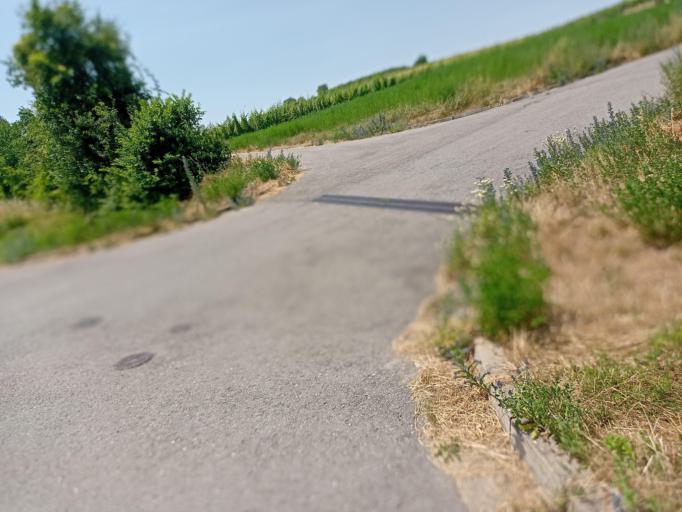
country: DE
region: Baden-Wuerttemberg
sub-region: Karlsruhe Region
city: Ubstadt-Weiher
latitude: 49.1749
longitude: 8.6638
